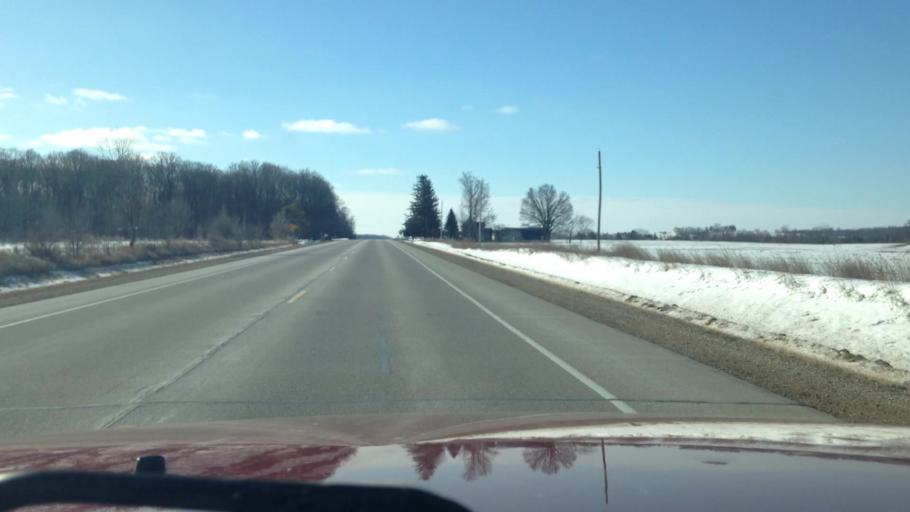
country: US
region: Wisconsin
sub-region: Waukesha County
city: Oconomowoc
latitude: 43.1895
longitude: -88.5081
